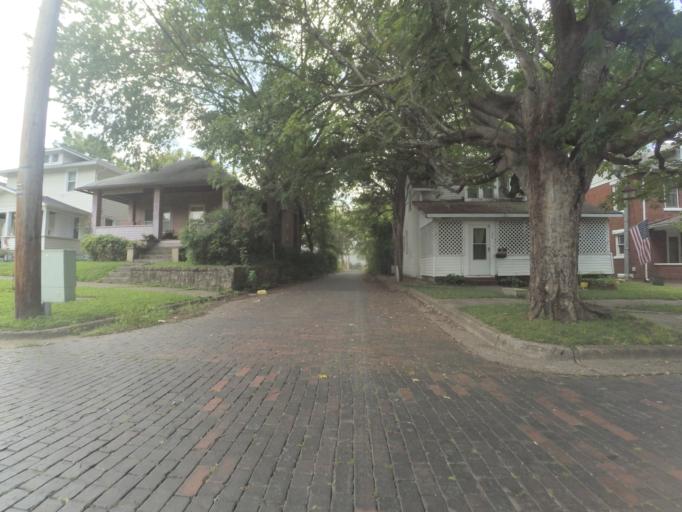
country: US
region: West Virginia
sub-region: Cabell County
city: Huntington
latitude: 38.4157
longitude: -82.4186
